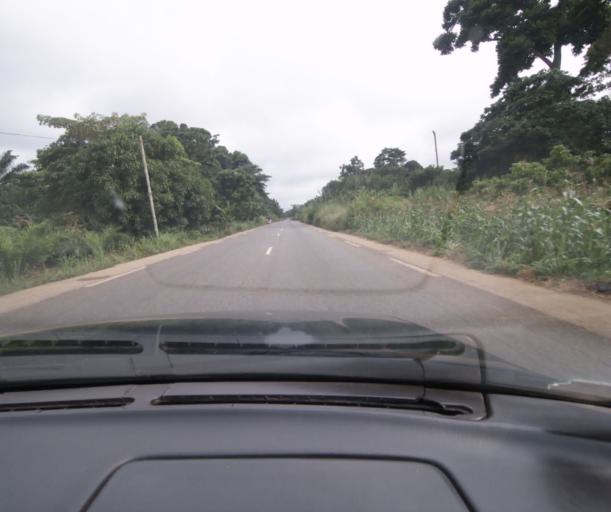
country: CM
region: Centre
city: Ombesa
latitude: 4.5943
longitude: 11.2608
